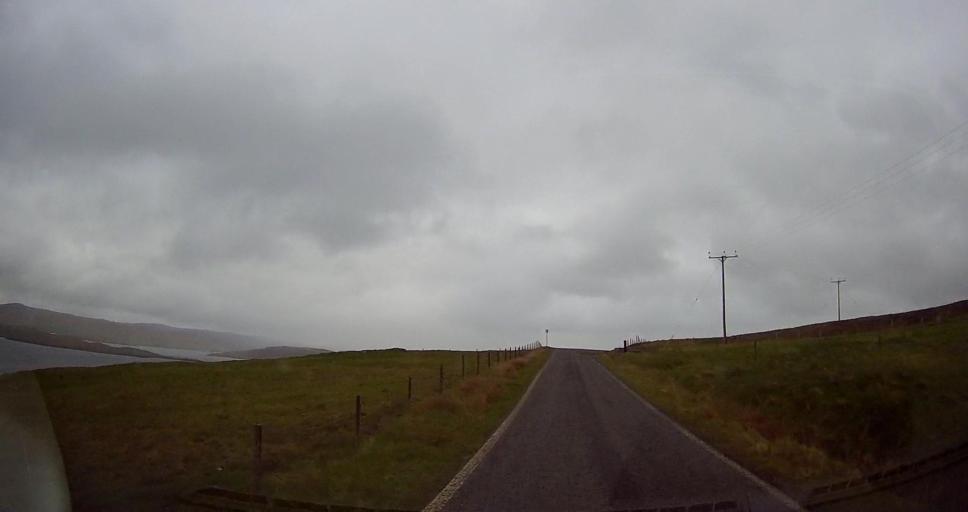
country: GB
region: Scotland
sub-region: Shetland Islands
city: Lerwick
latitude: 60.3819
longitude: -1.3792
